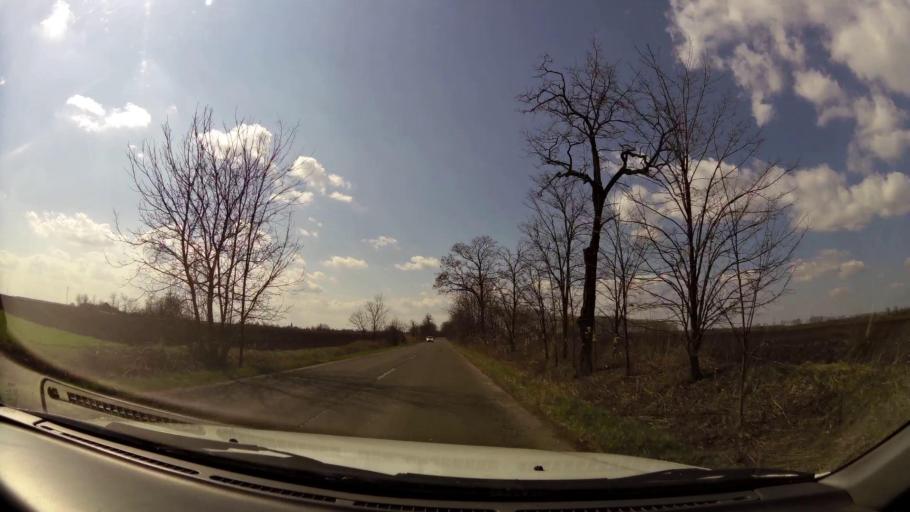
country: HU
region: Pest
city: Tapioszele
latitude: 47.3351
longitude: 19.9000
